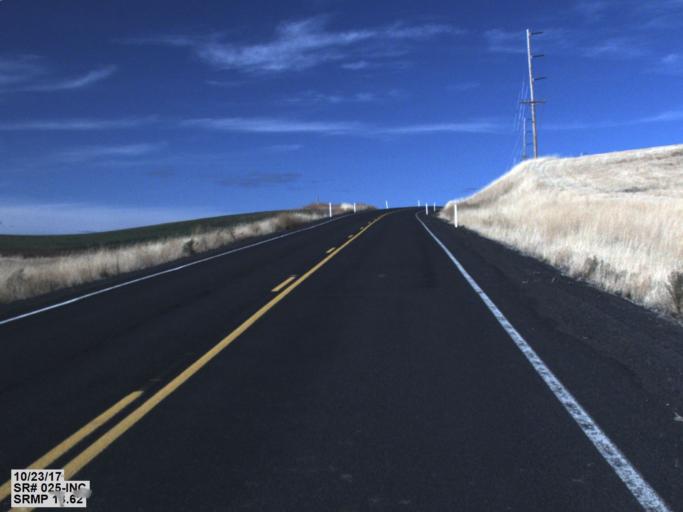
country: US
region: Washington
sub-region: Lincoln County
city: Davenport
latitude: 47.8323
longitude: -118.2101
